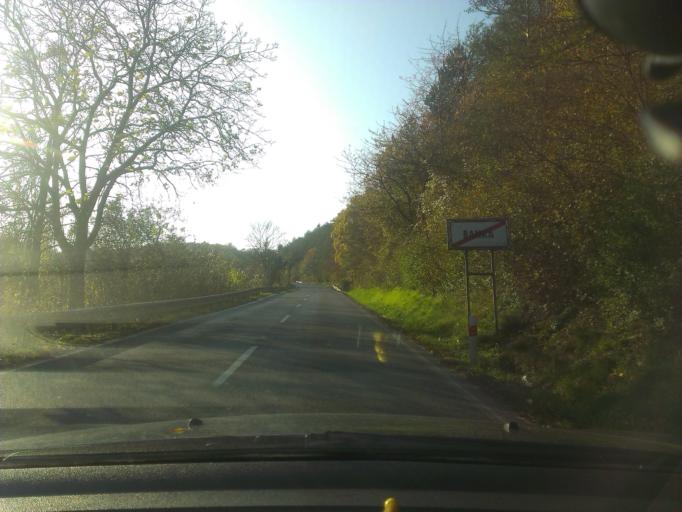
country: SK
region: Trnavsky
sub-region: Okres Trnava
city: Piestany
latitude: 48.5758
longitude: 17.8513
